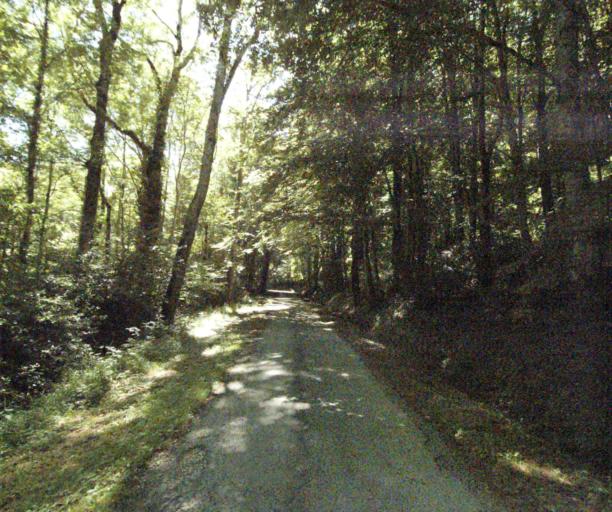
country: FR
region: Midi-Pyrenees
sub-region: Departement du Tarn
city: Dourgne
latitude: 43.4333
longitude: 2.1604
